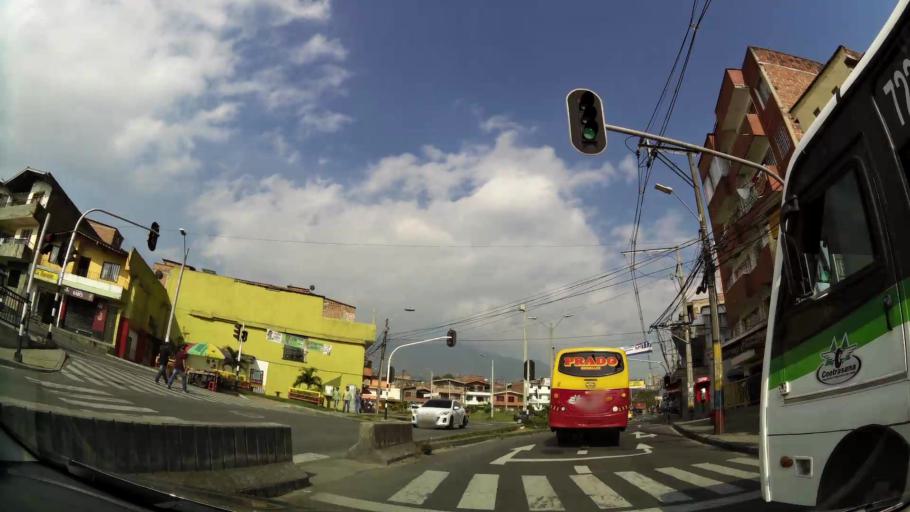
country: CO
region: Antioquia
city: La Estrella
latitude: 6.1740
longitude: -75.6335
